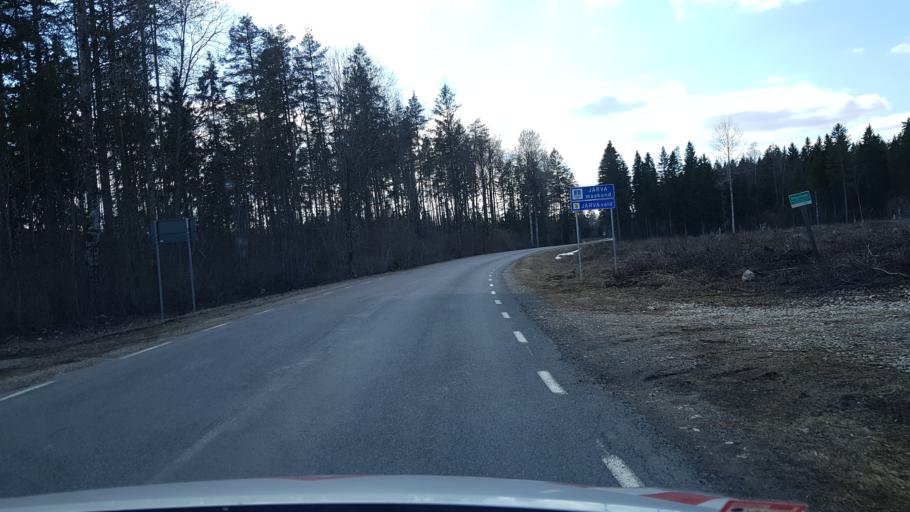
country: EE
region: Laeaene-Virumaa
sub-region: Tapa vald
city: Tapa
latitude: 59.1811
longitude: 26.0093
